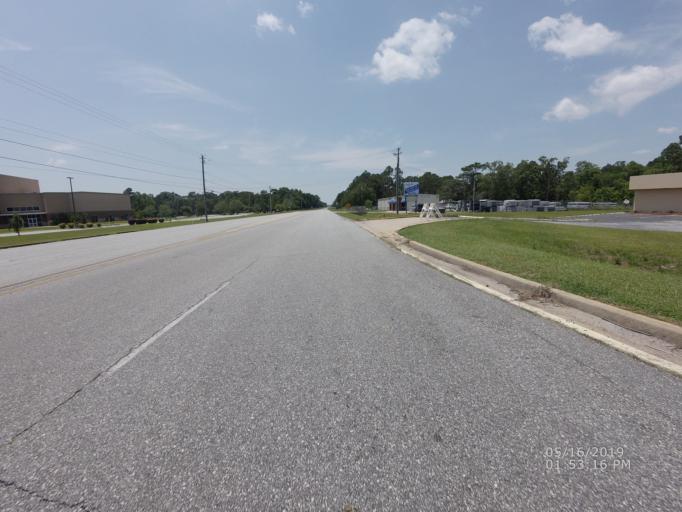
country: US
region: Georgia
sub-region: Dougherty County
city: Albany
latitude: 31.5491
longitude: -84.2247
